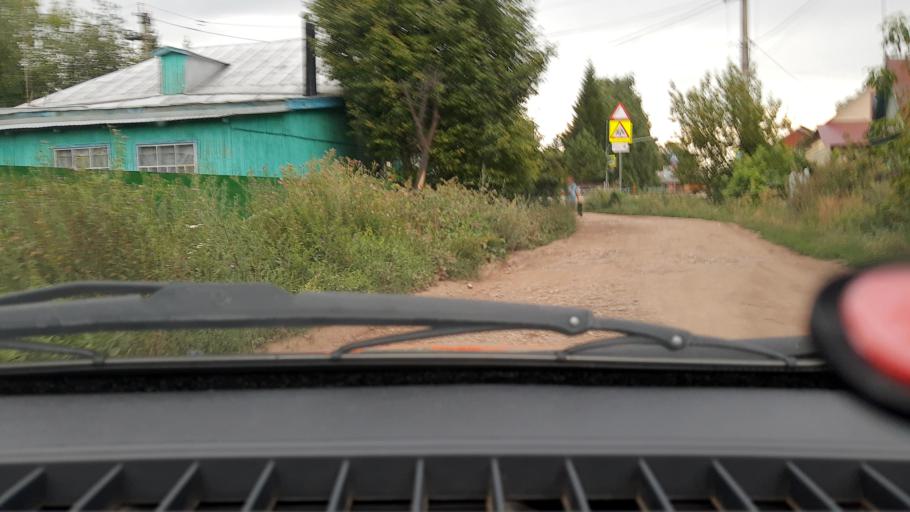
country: RU
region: Bashkortostan
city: Chishmy
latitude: 54.5930
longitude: 55.4042
